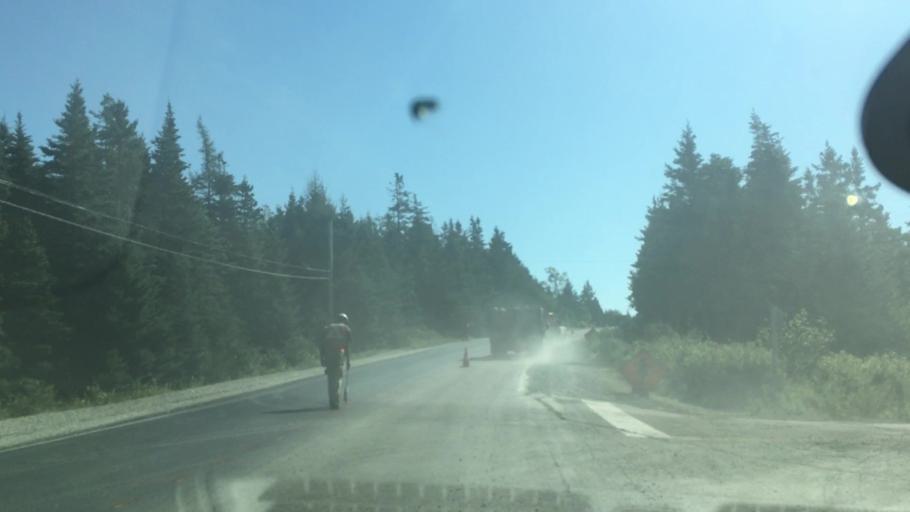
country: CA
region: Nova Scotia
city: New Glasgow
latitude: 44.9067
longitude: -62.4918
